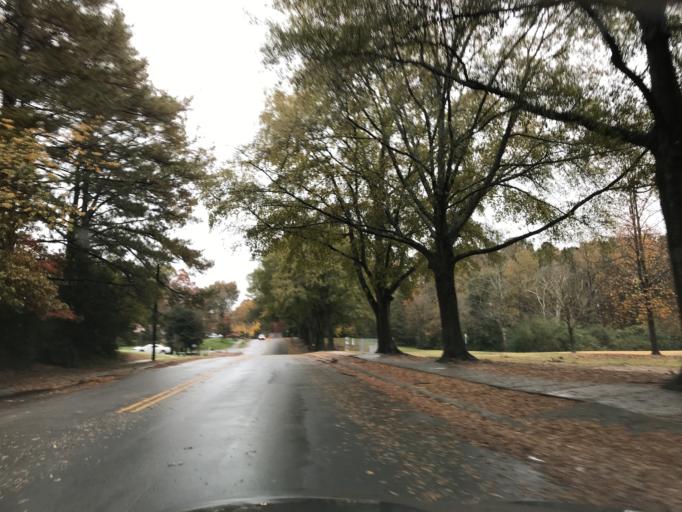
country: US
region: North Carolina
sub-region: Wake County
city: West Raleigh
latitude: 35.8396
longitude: -78.6216
